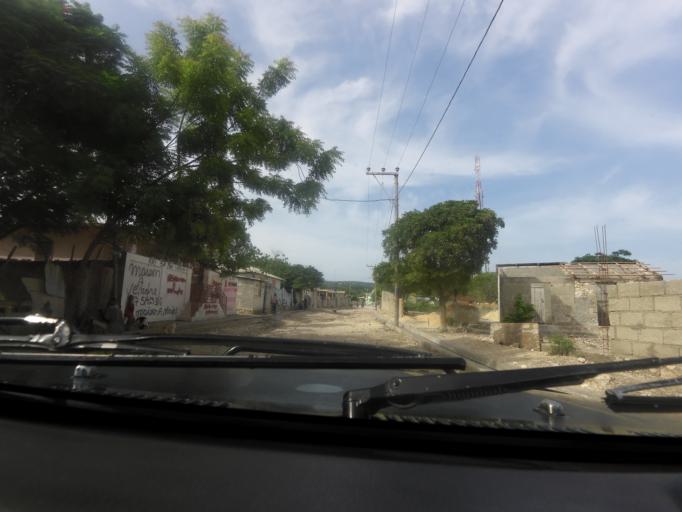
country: HT
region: Ouest
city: Anse a Galets
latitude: 18.8352
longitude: -72.8631
